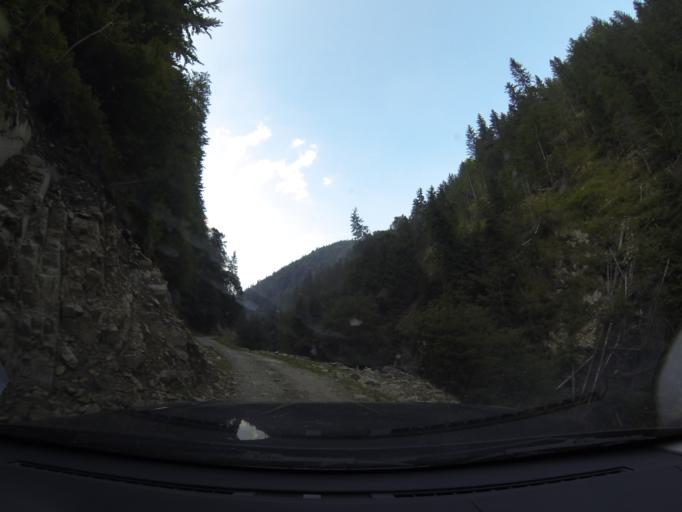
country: RO
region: Arges
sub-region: Comuna Arefu
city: Arefu
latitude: 45.5177
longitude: 24.6792
